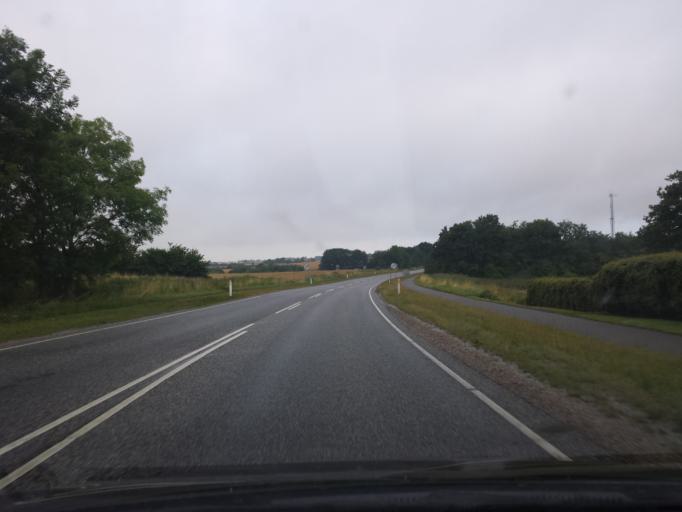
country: DK
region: South Denmark
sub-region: Sonderborg Kommune
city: Guderup
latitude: 54.9889
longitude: 9.8607
